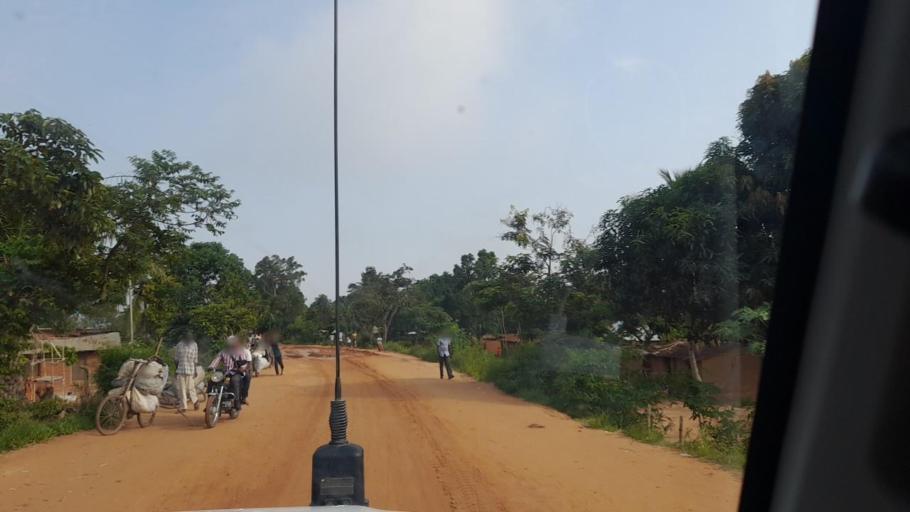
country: CD
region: Kasai-Occidental
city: Kananga
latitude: -5.8924
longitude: 22.3756
